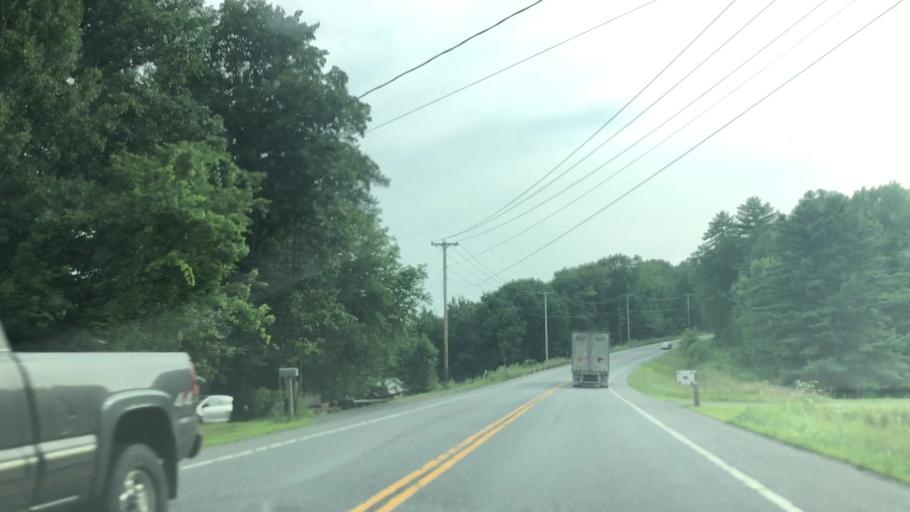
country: US
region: New York
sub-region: Warren County
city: Glens Falls North
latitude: 43.3774
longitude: -73.6618
